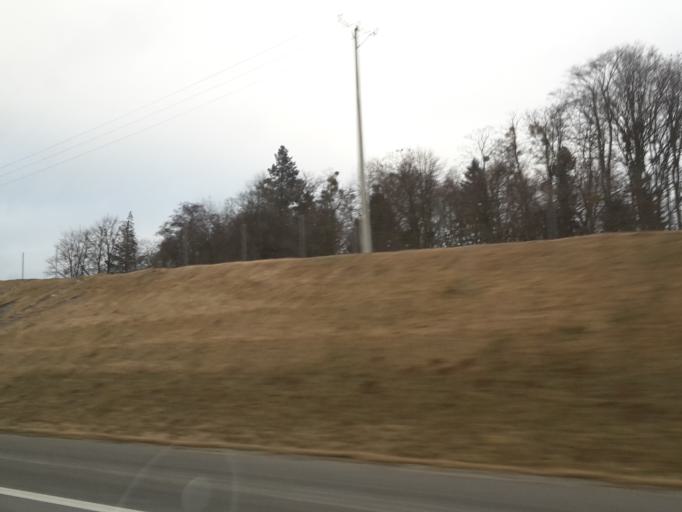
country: PL
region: Warmian-Masurian Voivodeship
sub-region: Powiat ostrodzki
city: Maldyty
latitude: 53.8585
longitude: 19.7496
